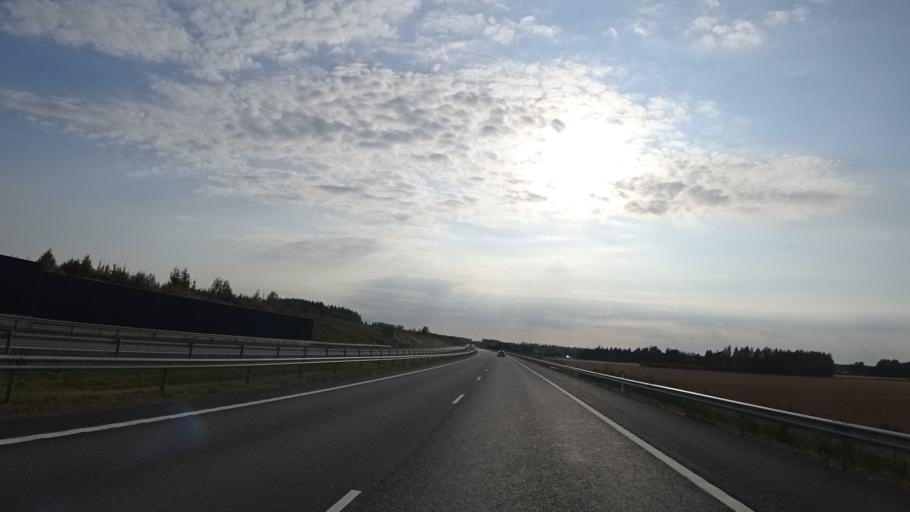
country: FI
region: Kymenlaakso
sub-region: Kotka-Hamina
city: Broby
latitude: 60.5027
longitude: 26.7166
